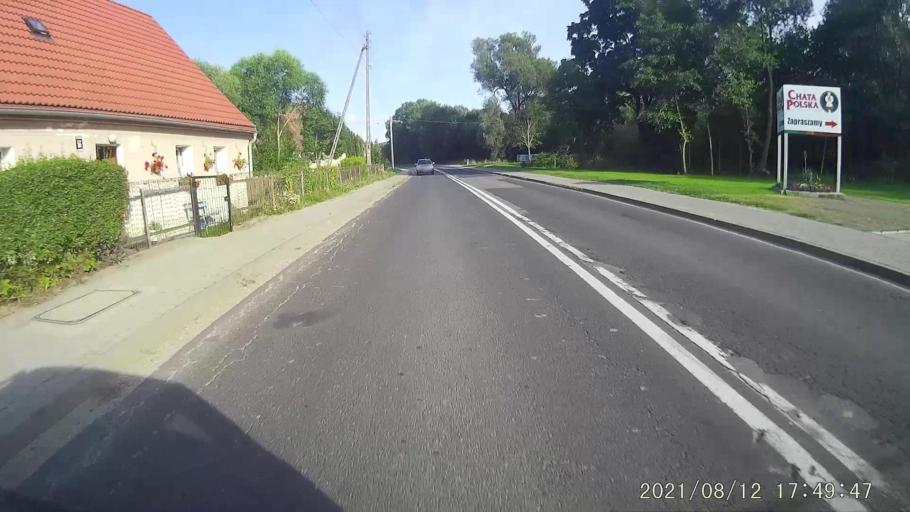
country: PL
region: Lower Silesian Voivodeship
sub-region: Powiat klodzki
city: Klodzko
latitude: 50.3620
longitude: 16.7151
